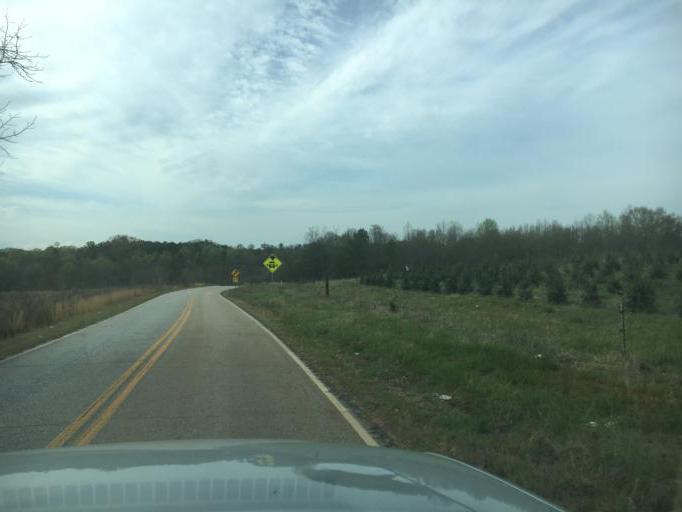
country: US
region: South Carolina
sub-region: Spartanburg County
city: Duncan
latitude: 34.9293
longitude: -82.1651
